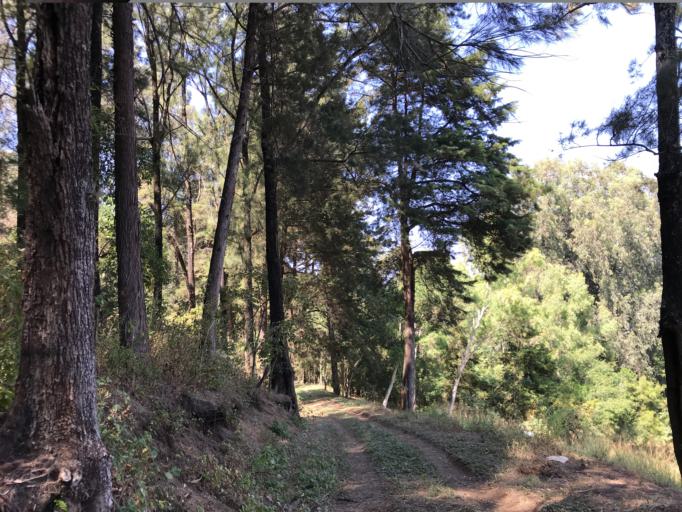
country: GT
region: Guatemala
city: Villa Canales
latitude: 14.4812
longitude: -90.5458
